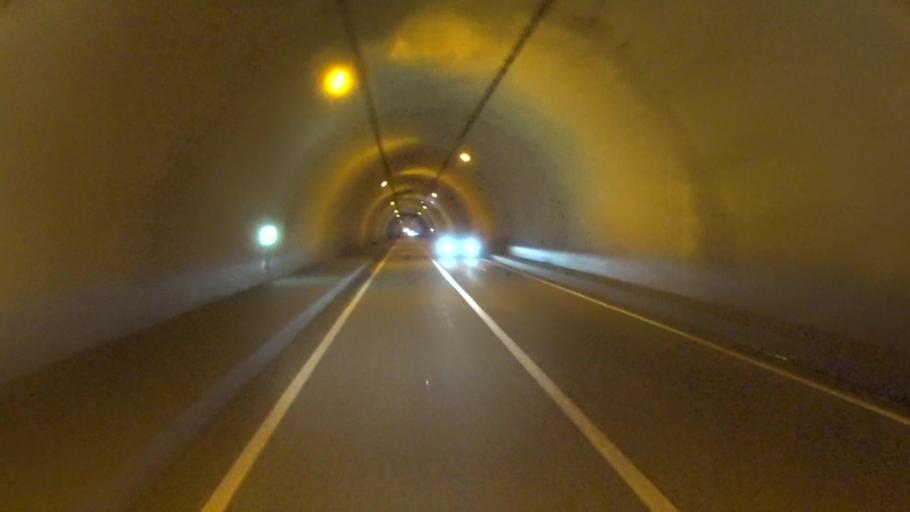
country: JP
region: Kyoto
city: Maizuru
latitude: 35.5113
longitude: 135.3808
